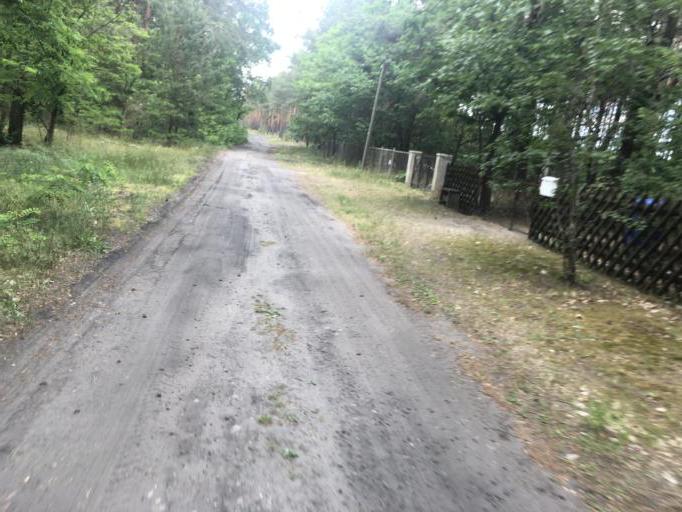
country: DE
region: Brandenburg
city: Gross Koris
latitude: 52.1865
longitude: 13.6506
